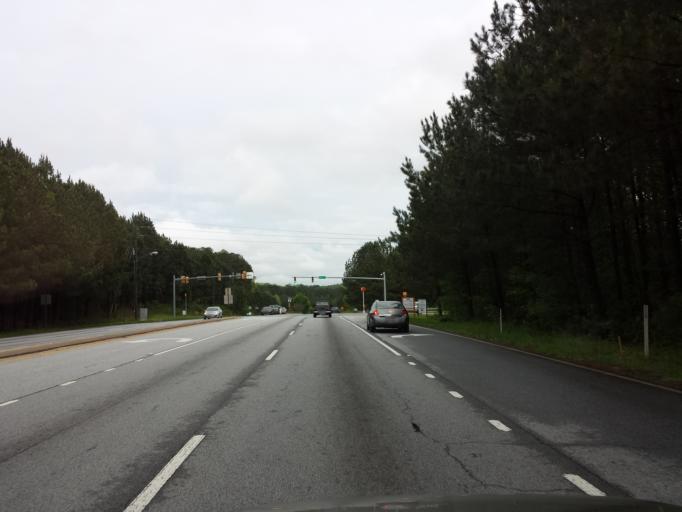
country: US
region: Georgia
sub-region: Cobb County
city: Smyrna
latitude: 33.8454
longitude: -84.5395
